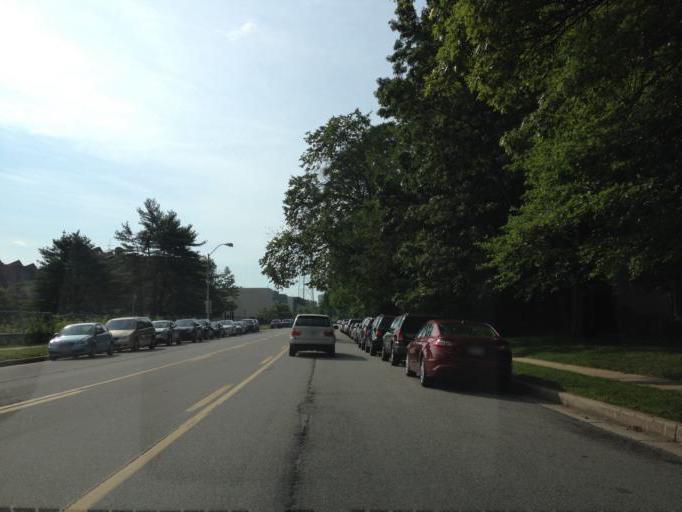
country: US
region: Maryland
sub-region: Baltimore County
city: Towson
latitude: 39.4079
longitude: -76.6114
